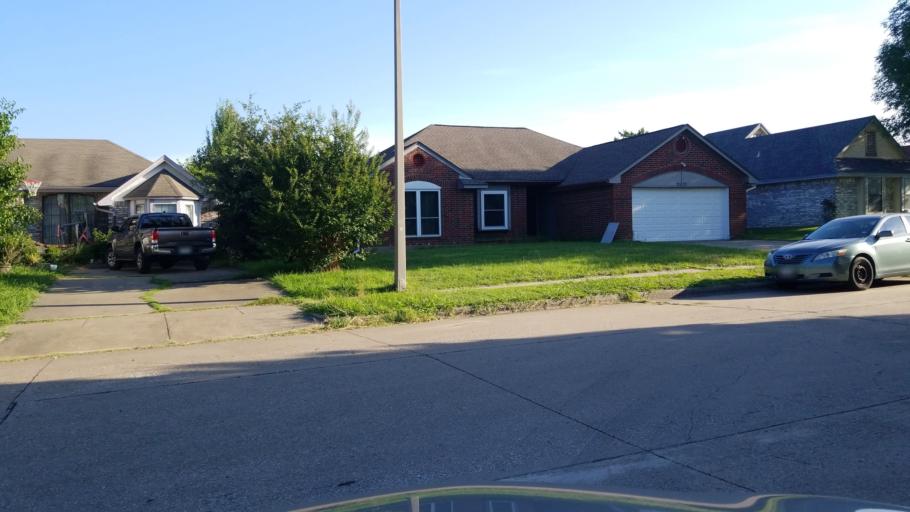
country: US
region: Texas
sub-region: Dallas County
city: Grand Prairie
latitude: 32.6812
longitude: -97.0416
